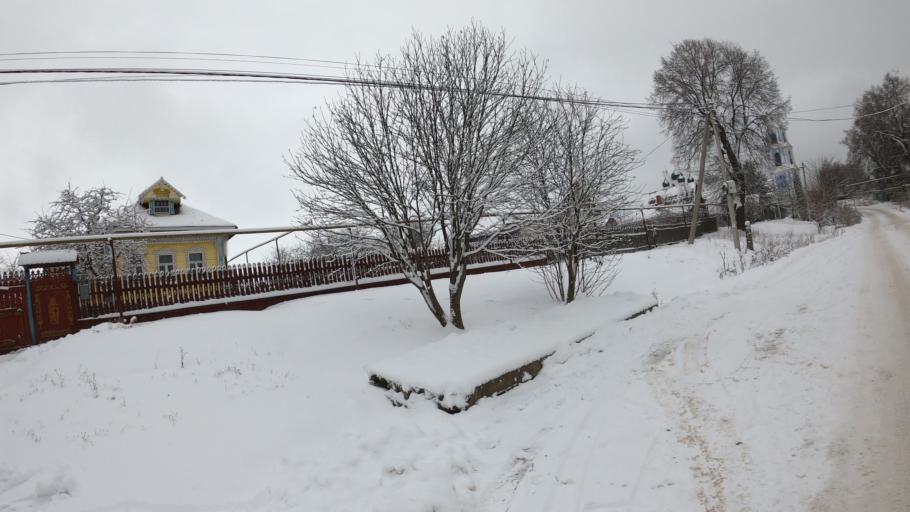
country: RU
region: Jaroslavl
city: Pereslavl'-Zalesskiy
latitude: 56.7591
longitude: 38.8603
